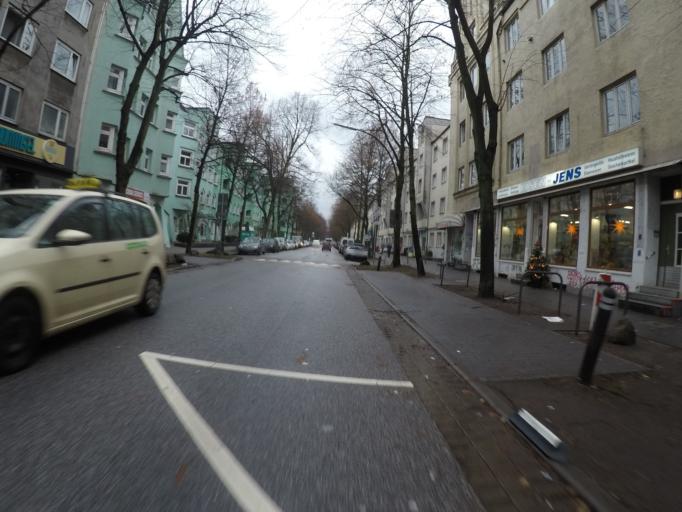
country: DE
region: Hamburg
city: Kleiner Grasbrook
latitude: 53.5140
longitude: 9.9871
